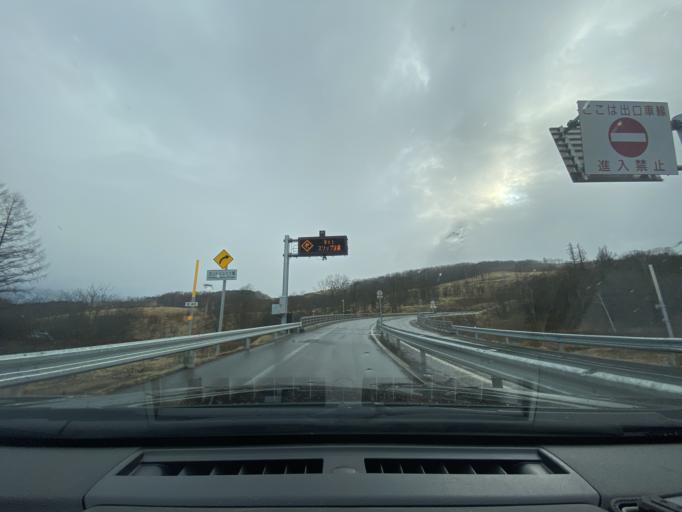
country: JP
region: Hokkaido
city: Kitami
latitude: 43.5888
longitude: 143.6775
